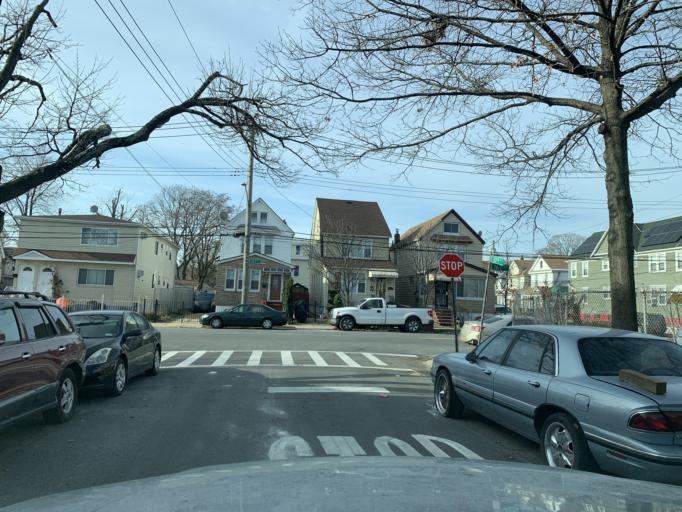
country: US
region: New York
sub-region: Queens County
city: Jamaica
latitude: 40.6955
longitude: -73.7859
